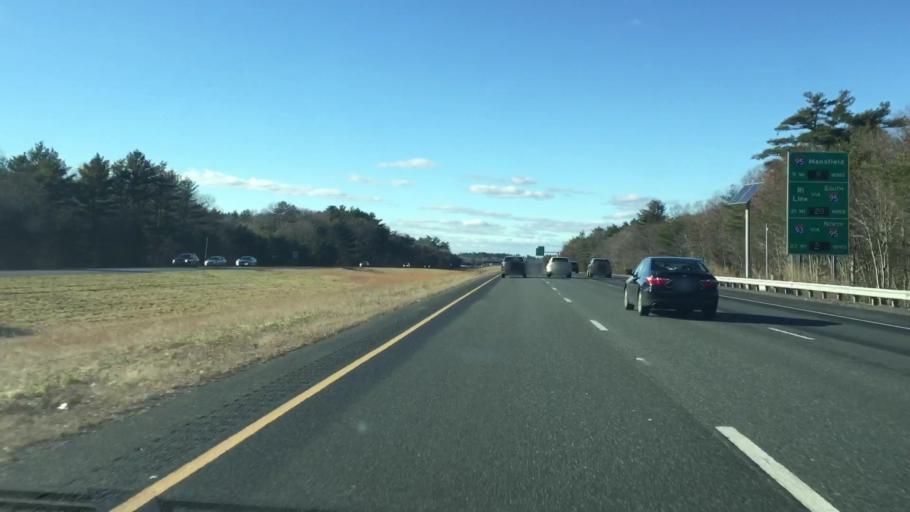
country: US
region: Massachusetts
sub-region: Bristol County
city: Raynham
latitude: 41.9616
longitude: -71.1070
